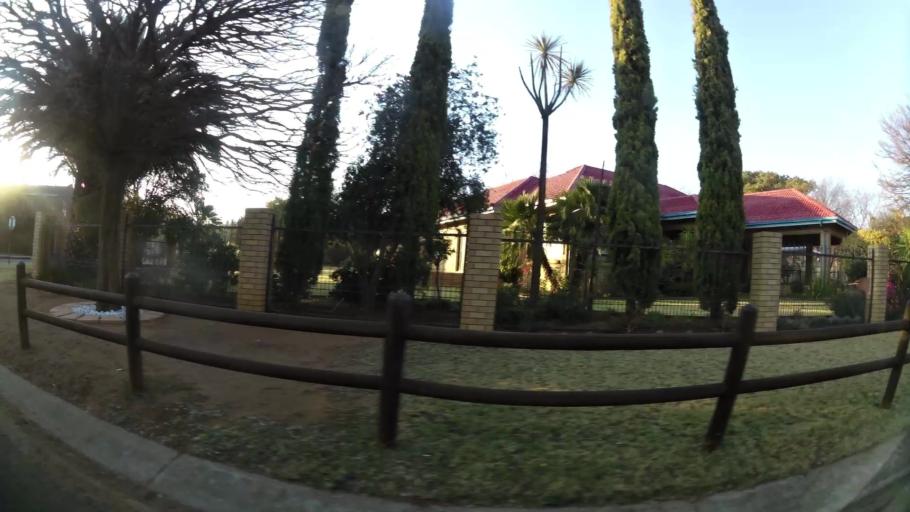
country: ZA
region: Orange Free State
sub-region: Mangaung Metropolitan Municipality
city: Bloemfontein
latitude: -29.0908
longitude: 26.1539
